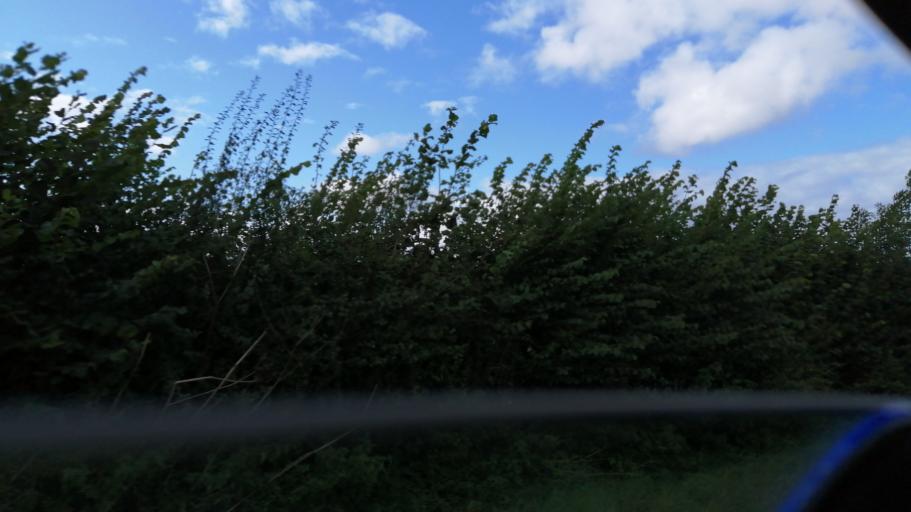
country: GB
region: England
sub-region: Herefordshire
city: Callow
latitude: 52.0227
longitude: -2.7254
